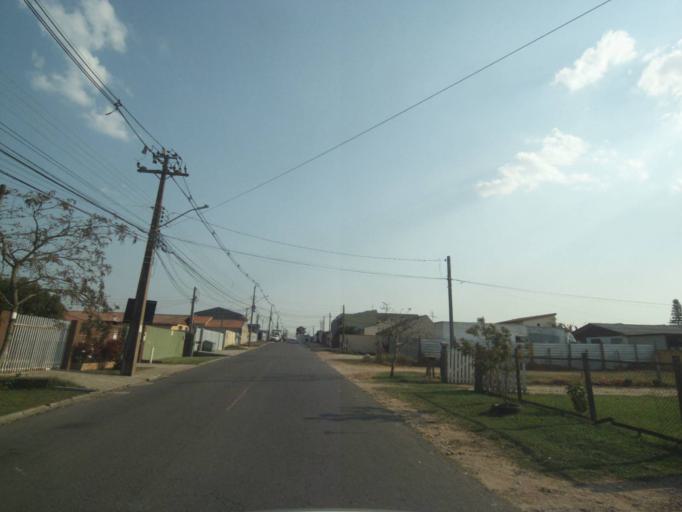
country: BR
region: Parana
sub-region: Sao Jose Dos Pinhais
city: Sao Jose dos Pinhais
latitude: -25.5309
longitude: -49.2366
